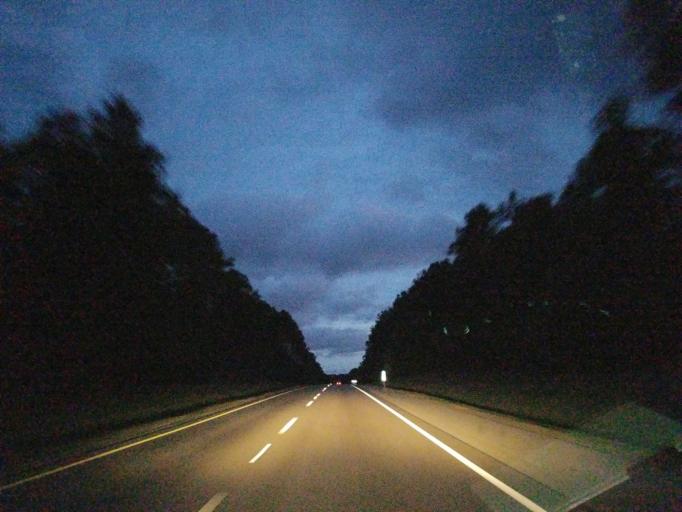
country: US
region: Mississippi
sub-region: Jones County
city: Sharon
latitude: 31.8616
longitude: -89.0473
